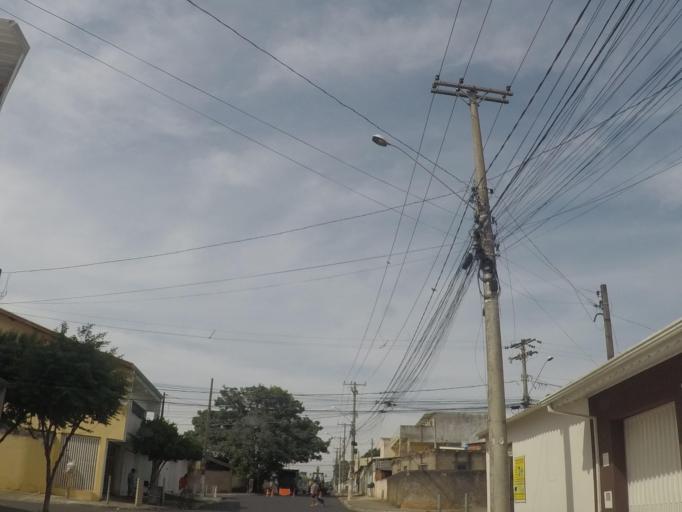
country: BR
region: Sao Paulo
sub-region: Hortolandia
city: Hortolandia
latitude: -22.8466
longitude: -47.1953
